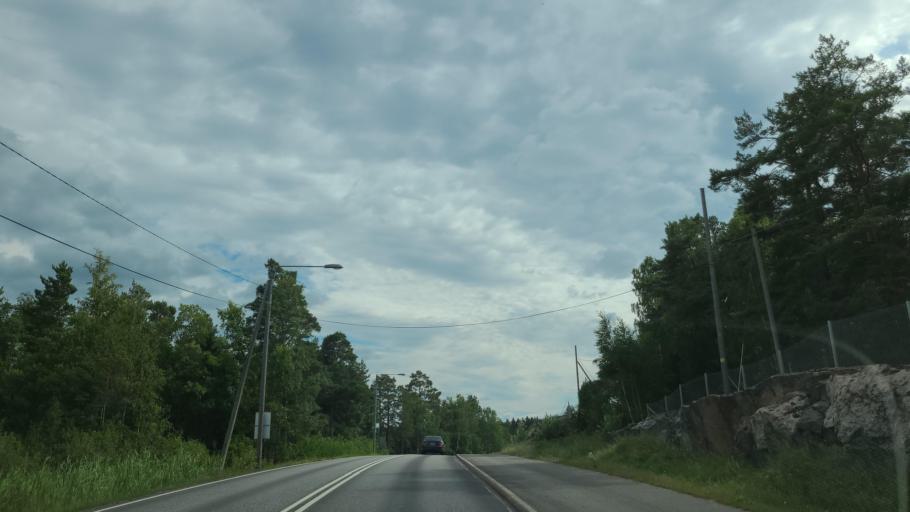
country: FI
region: Varsinais-Suomi
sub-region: Turku
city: Rymaettylae
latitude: 60.4122
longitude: 21.8981
